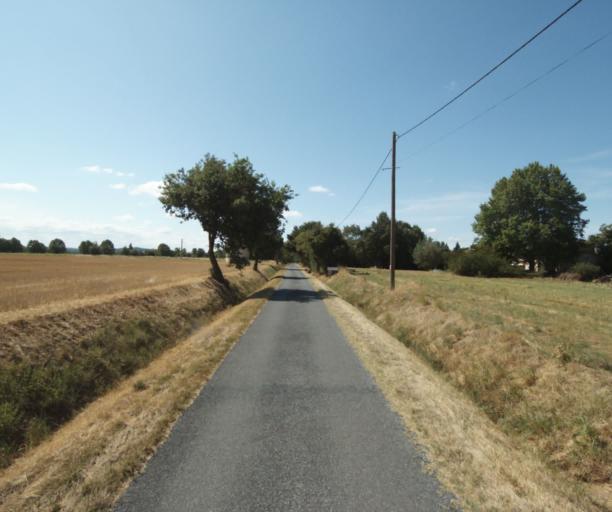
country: FR
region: Midi-Pyrenees
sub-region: Departement de la Haute-Garonne
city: Revel
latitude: 43.4993
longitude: 2.0015
